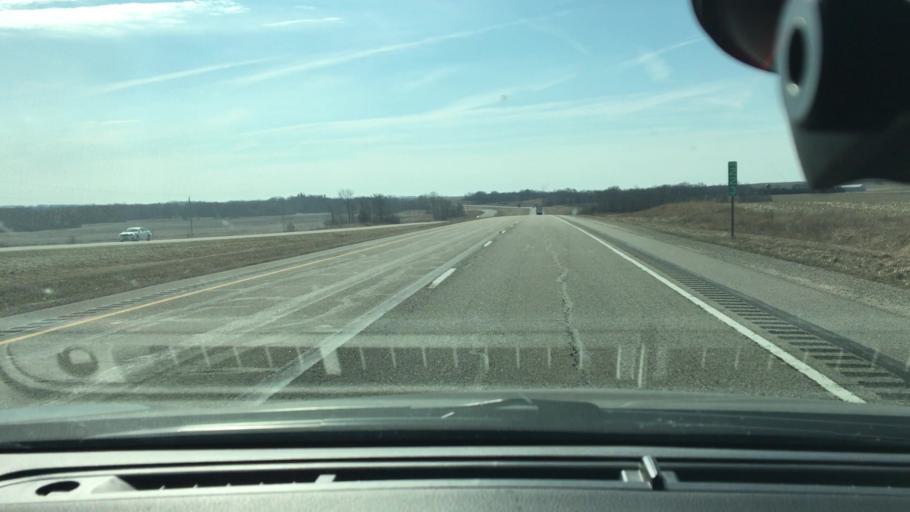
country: US
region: Iowa
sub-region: Chickasaw County
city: Nashua
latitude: 42.9867
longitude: -92.5875
